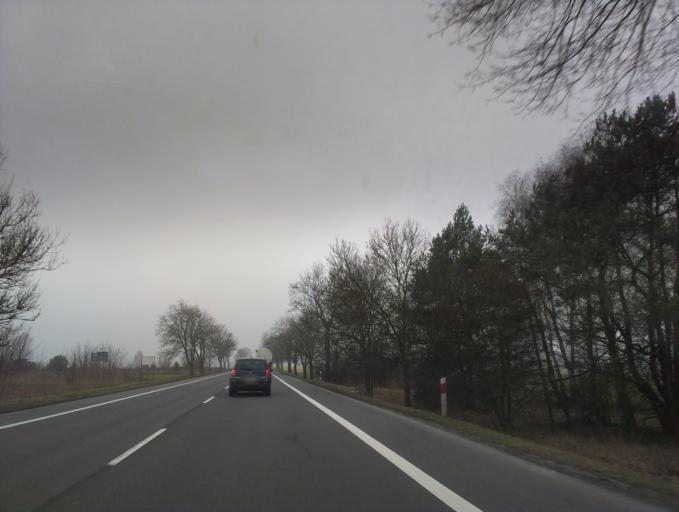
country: PL
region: Greater Poland Voivodeship
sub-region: Powiat pilski
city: Ujscie
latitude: 53.0934
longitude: 16.7393
